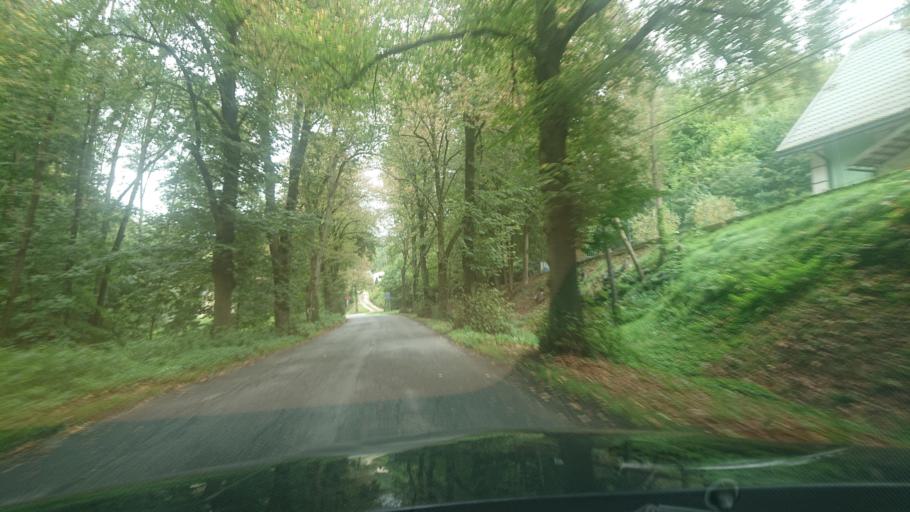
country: PL
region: Lower Silesian Voivodeship
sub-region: Powiat klodzki
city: Bystrzyca Klodzka
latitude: 50.3195
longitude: 16.7143
